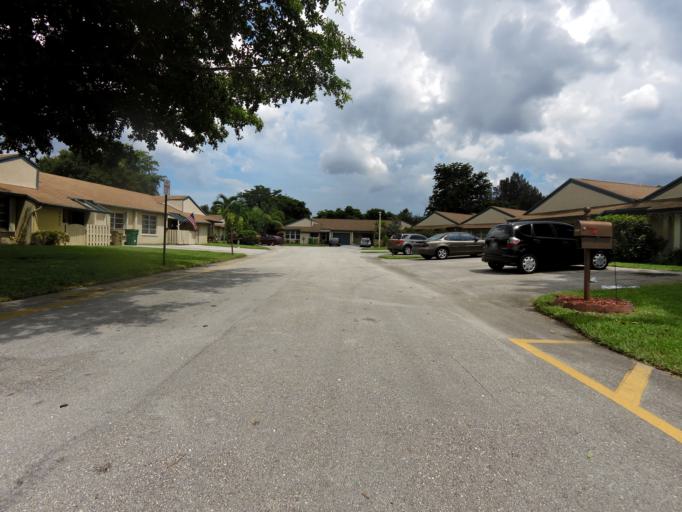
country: US
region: Florida
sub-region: Broward County
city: Cooper City
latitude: 26.0715
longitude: -80.2635
